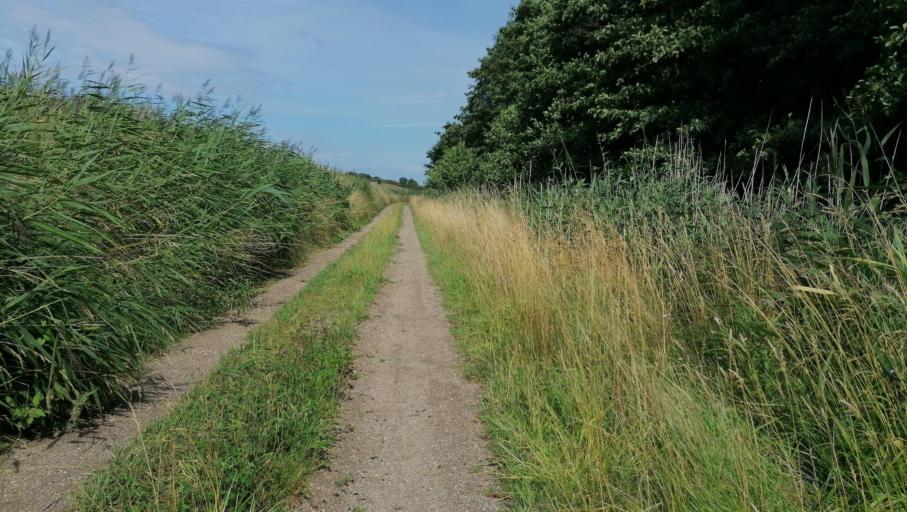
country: DK
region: Zealand
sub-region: Odsherred Kommune
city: Horve
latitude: 55.7876
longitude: 11.4223
